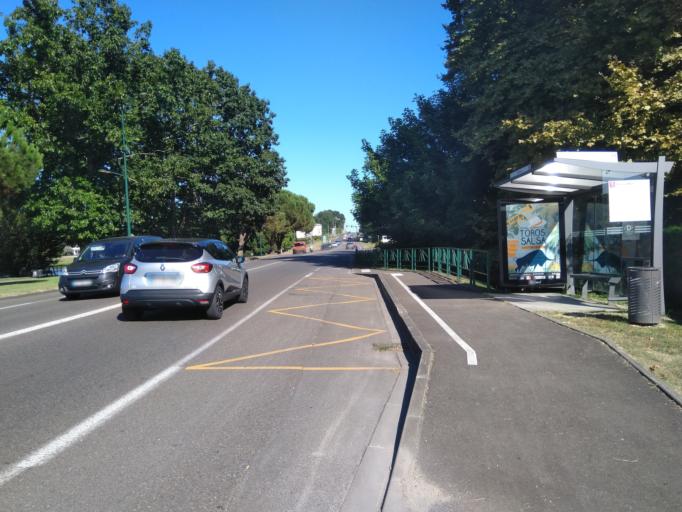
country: FR
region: Aquitaine
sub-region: Departement des Landes
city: Saint-Paul-les-Dax
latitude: 43.7255
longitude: -1.0683
